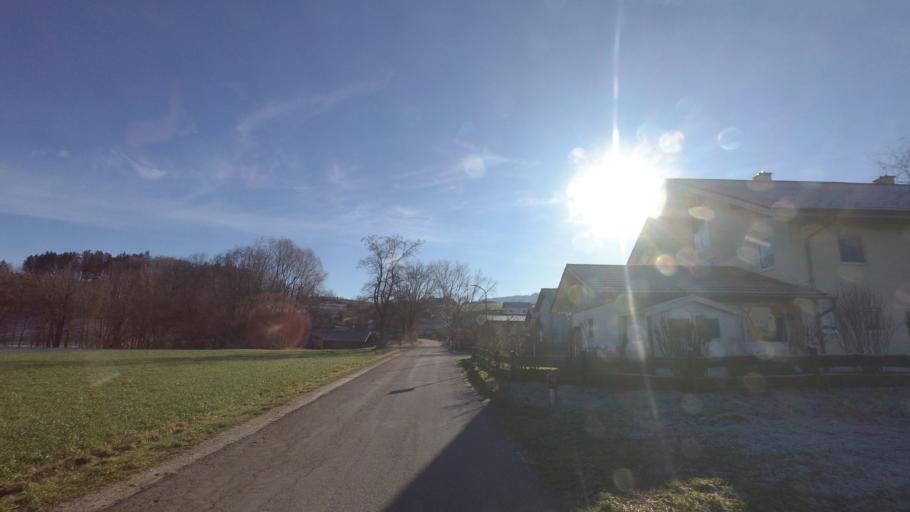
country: DE
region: Bavaria
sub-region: Upper Bavaria
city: Grabenstatt
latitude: 47.8405
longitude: 12.5457
